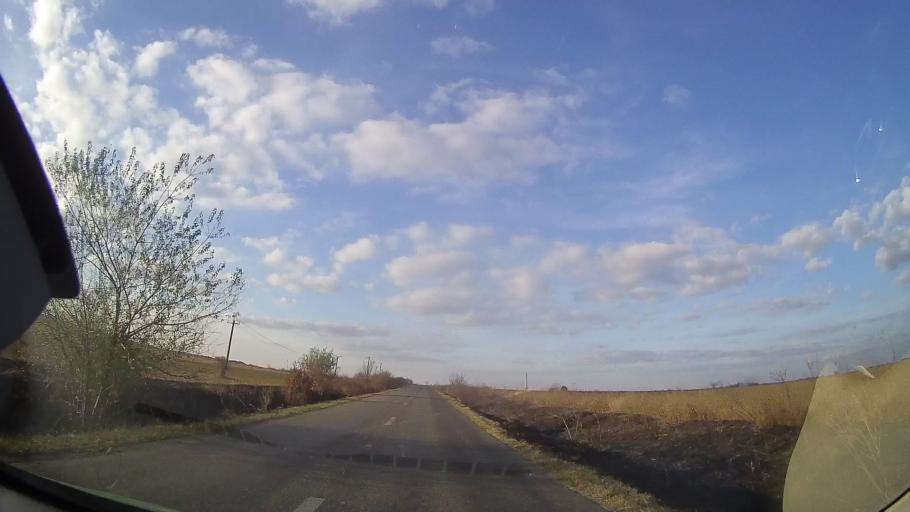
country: RO
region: Constanta
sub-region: Comuna Dumbraveni
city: Dumbraveni
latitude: 43.9318
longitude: 28.0266
